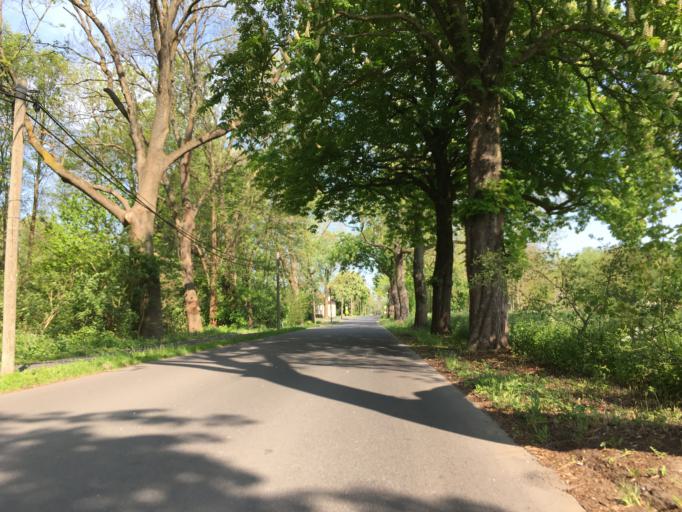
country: DE
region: Brandenburg
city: Altlandsberg
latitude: 52.5743
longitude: 13.7277
